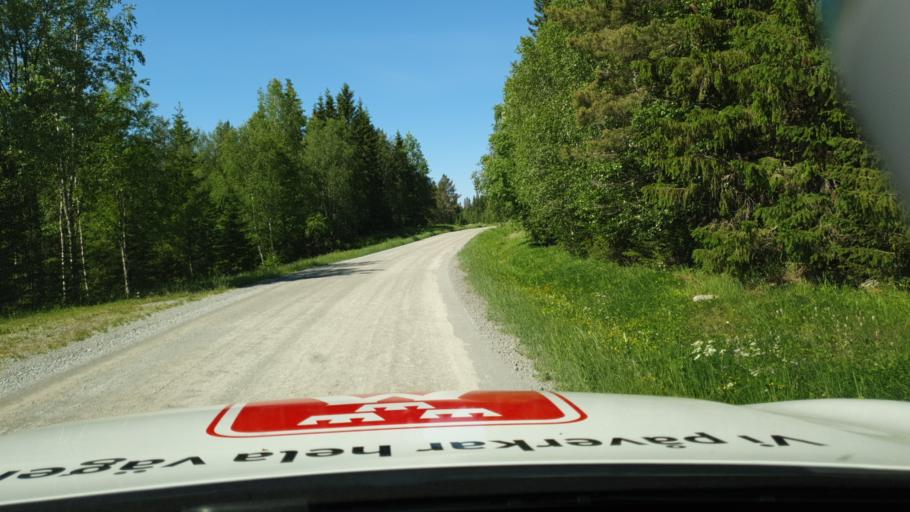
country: SE
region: Jaemtland
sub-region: Bergs Kommun
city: Hoverberg
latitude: 63.0299
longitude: 14.3579
